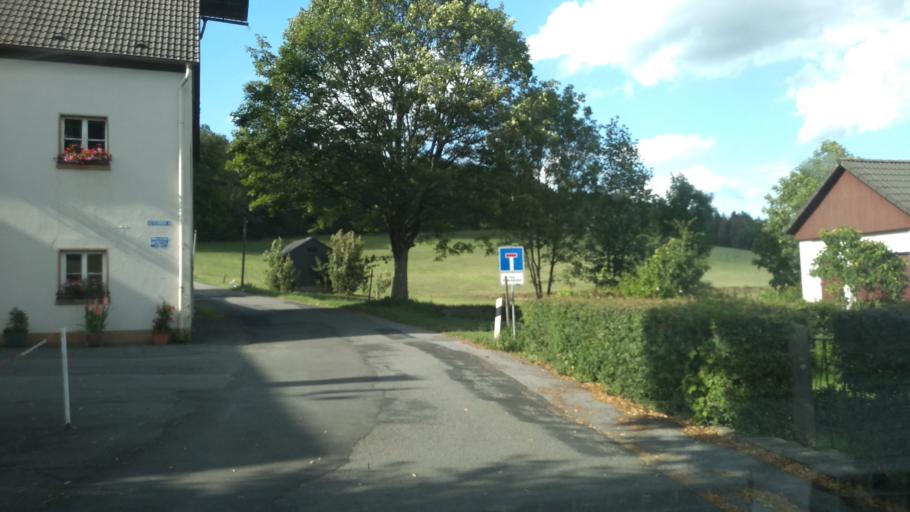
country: DE
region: North Rhine-Westphalia
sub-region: Regierungsbezirk Arnsberg
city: Schalksmuhle
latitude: 51.2109
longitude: 7.5527
